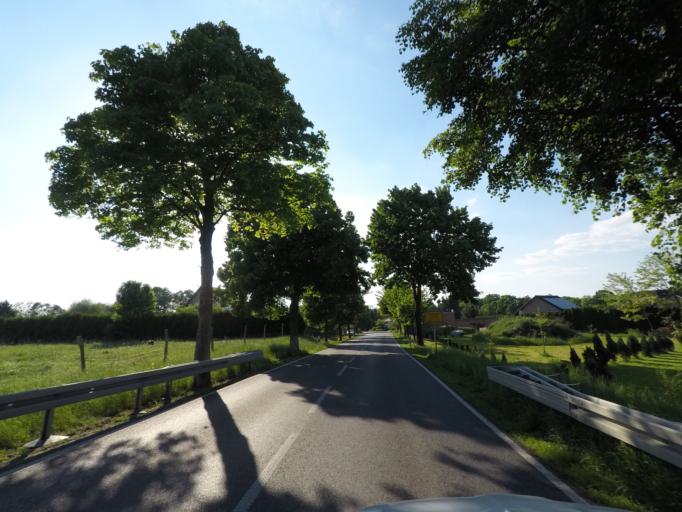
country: DE
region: Brandenburg
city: Hohenfinow
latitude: 52.8181
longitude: 13.8976
